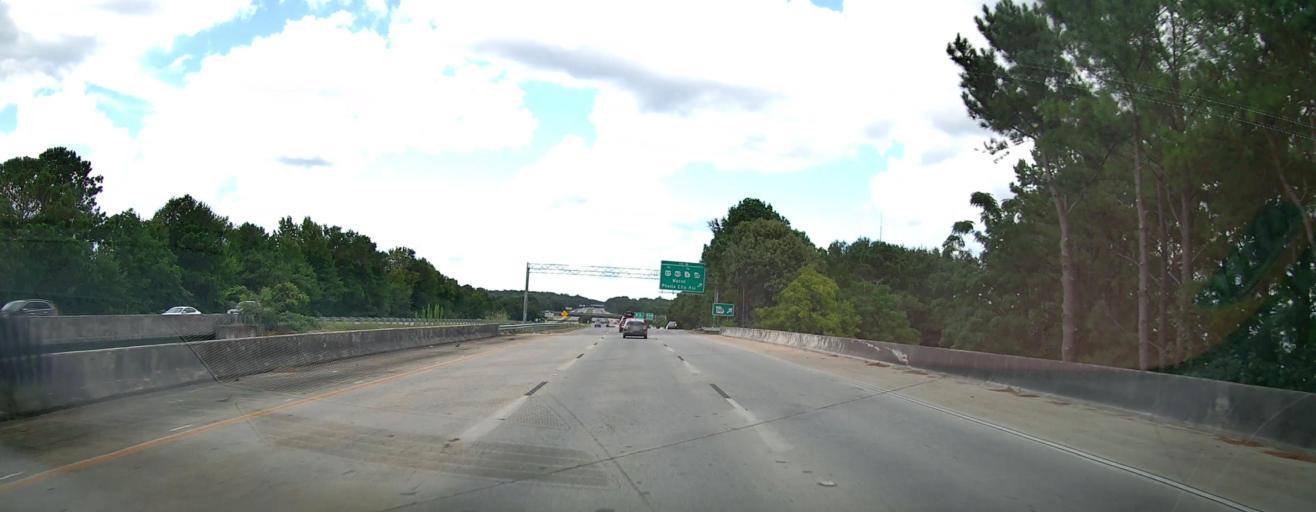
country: US
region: Alabama
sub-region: Russell County
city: Phenix City
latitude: 32.5370
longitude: -84.9594
